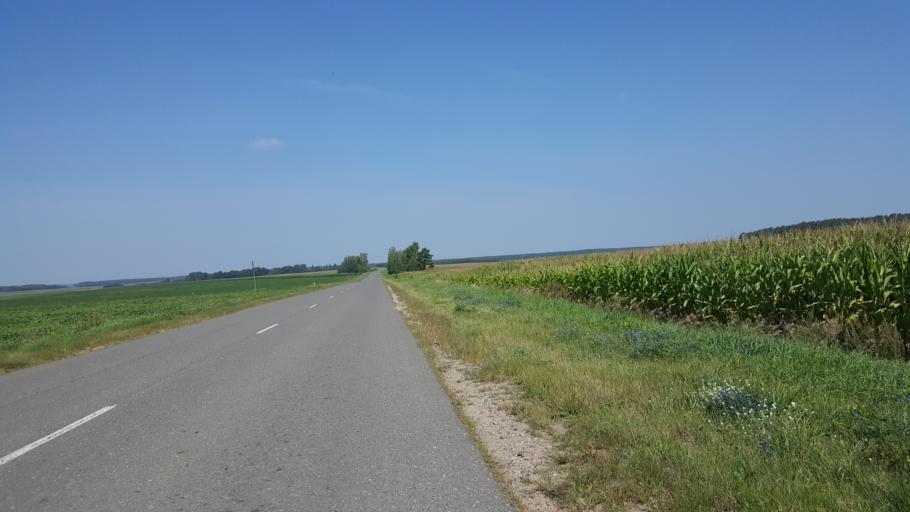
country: BY
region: Brest
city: Kamyanyuki
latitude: 52.4778
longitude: 23.7035
